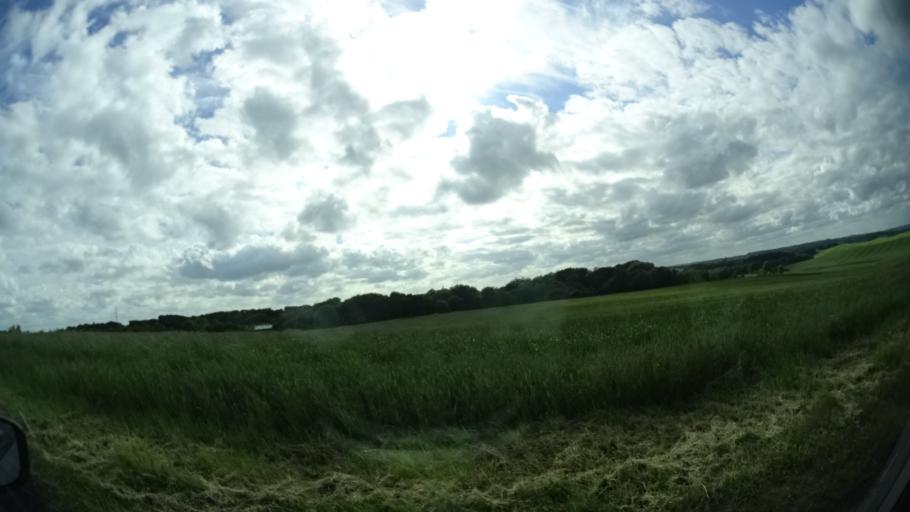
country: DK
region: Central Jutland
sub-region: Syddjurs Kommune
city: Ronde
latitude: 56.3265
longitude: 10.4353
